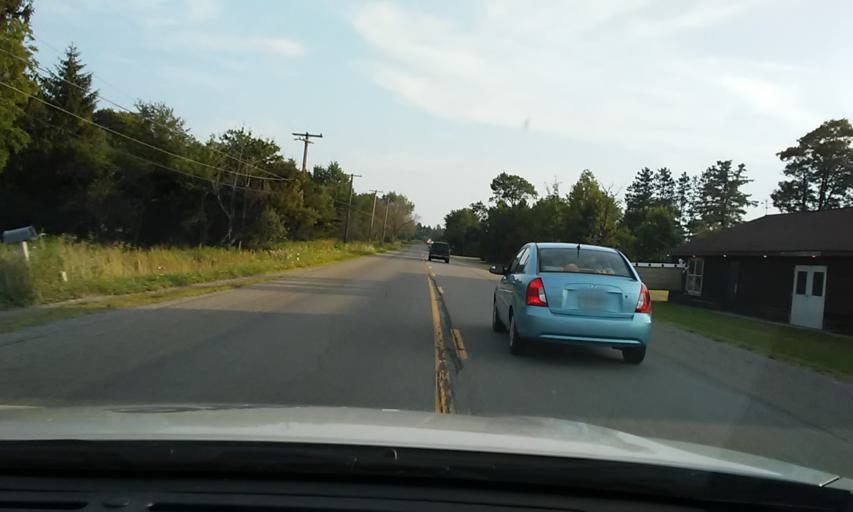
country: US
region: Pennsylvania
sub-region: McKean County
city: Kane
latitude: 41.6840
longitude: -78.7230
